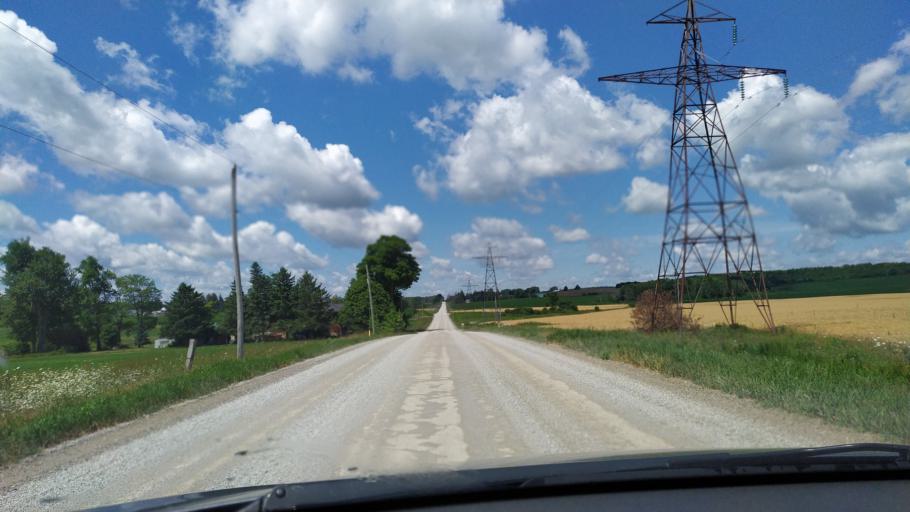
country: CA
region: Ontario
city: Stratford
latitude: 43.3874
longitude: -80.7654
